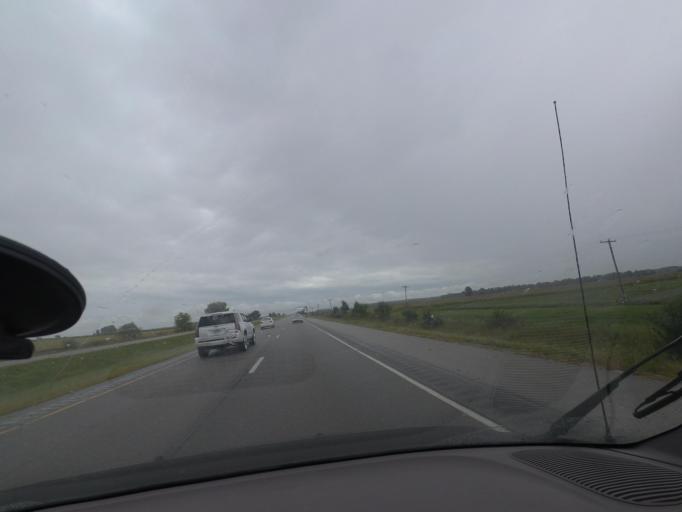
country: US
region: Indiana
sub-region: Fountain County
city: Veedersburg
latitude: 40.1196
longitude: -87.1412
